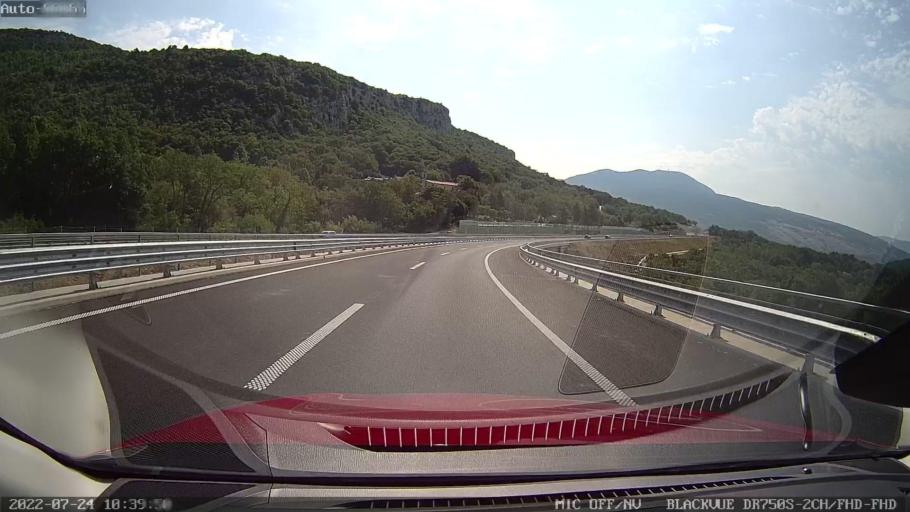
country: HR
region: Istarska
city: Lovran
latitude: 45.3400
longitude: 14.1247
